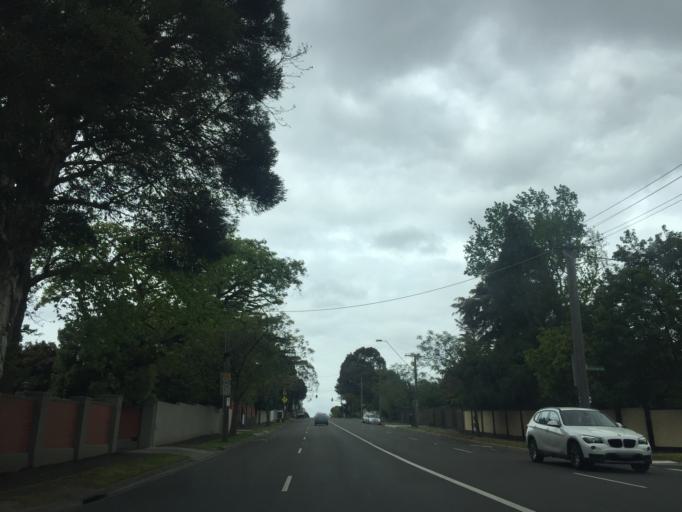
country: AU
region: Victoria
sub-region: Boroondara
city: Hawthorn East
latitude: -37.8162
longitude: 145.0500
